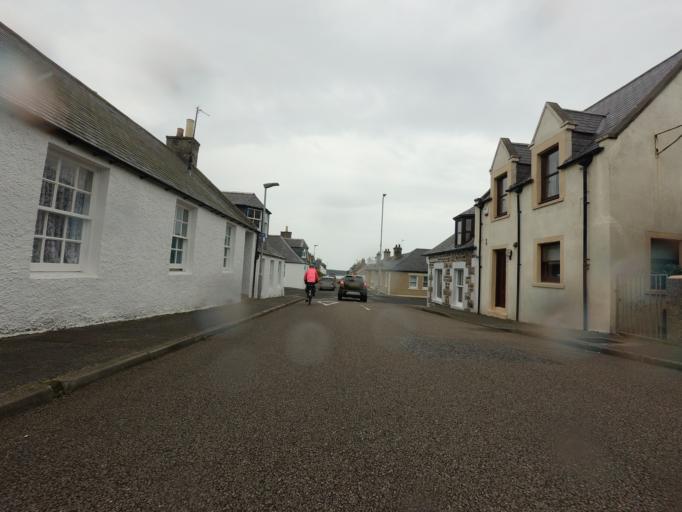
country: GB
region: Scotland
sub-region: Moray
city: Cullen
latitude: 57.6898
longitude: -2.8211
